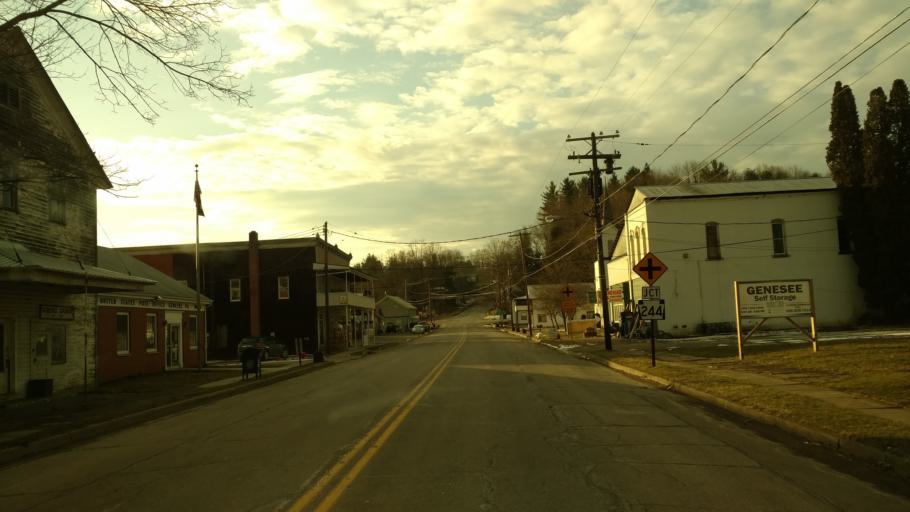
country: US
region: New York
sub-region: Allegany County
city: Wellsville
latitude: 41.9903
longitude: -77.8695
